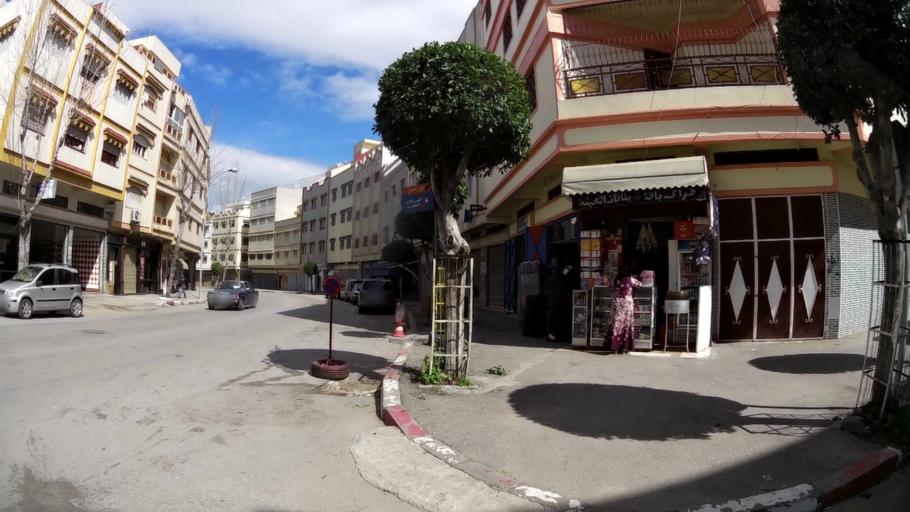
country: MA
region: Tanger-Tetouan
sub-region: Tanger-Assilah
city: Tangier
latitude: 35.7535
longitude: -5.8031
